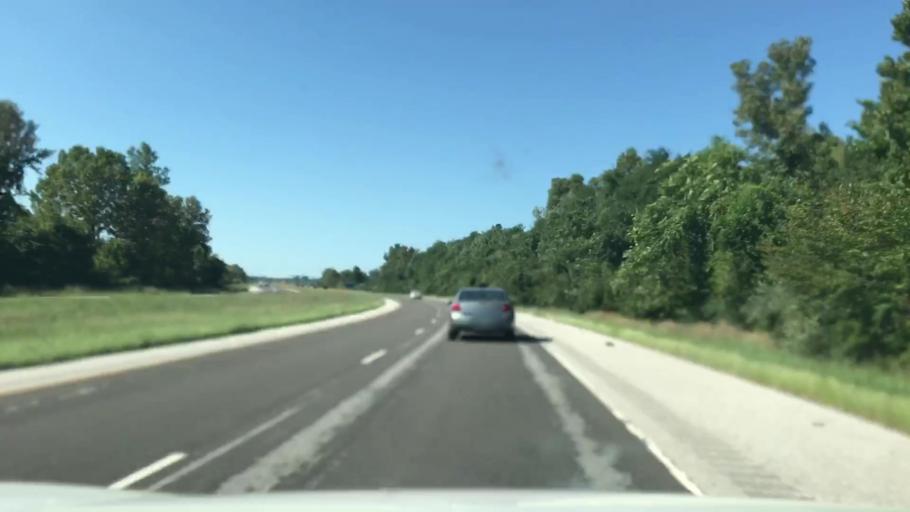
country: US
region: Illinois
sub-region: Madison County
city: South Roxana
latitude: 38.8406
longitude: -90.0439
